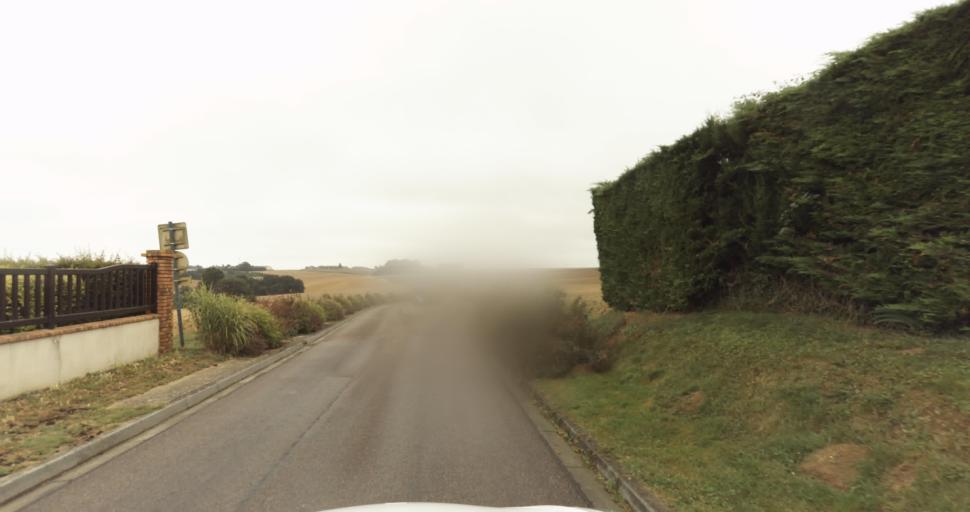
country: FR
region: Haute-Normandie
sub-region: Departement de l'Eure
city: Gravigny
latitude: 49.0805
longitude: 1.2121
